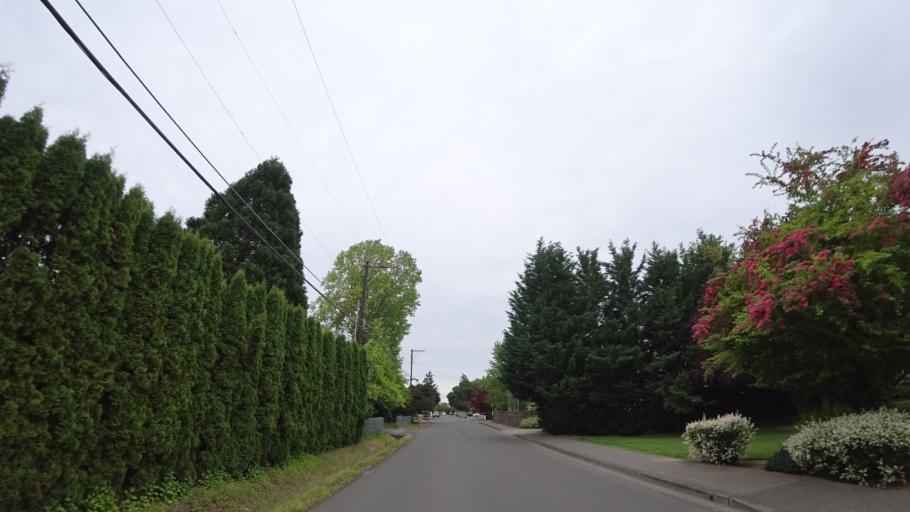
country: US
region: Oregon
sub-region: Washington County
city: Rockcreek
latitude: 45.5155
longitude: -122.9146
